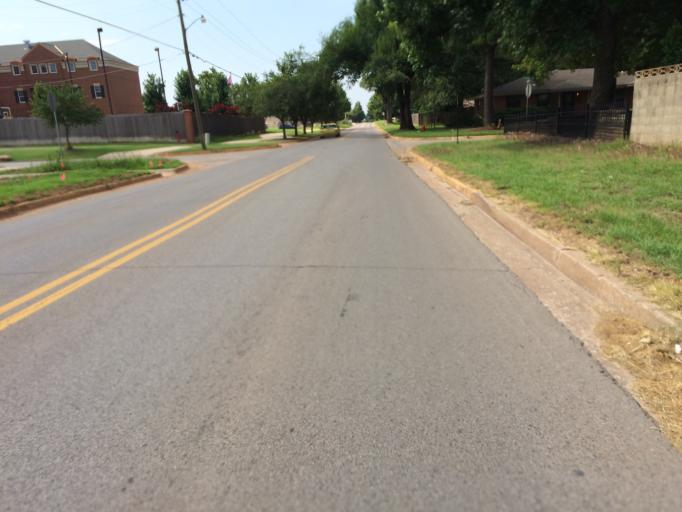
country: US
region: Oklahoma
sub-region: Cleveland County
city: Norman
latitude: 35.2012
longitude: -97.4502
